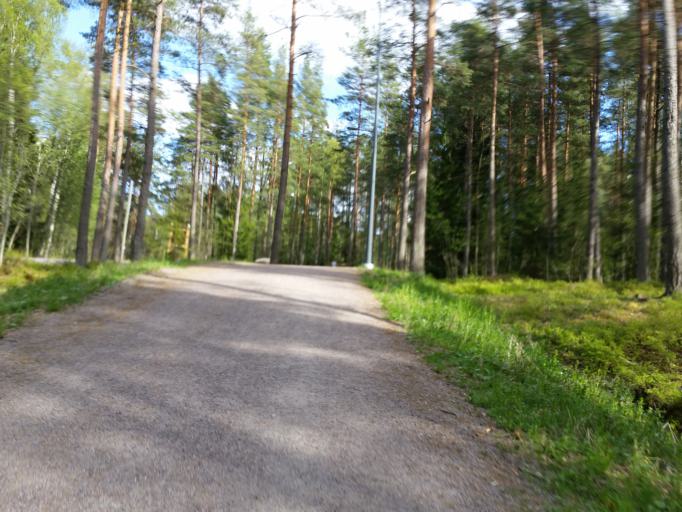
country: FI
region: Uusimaa
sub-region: Helsinki
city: Kauniainen
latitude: 60.1793
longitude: 24.7230
